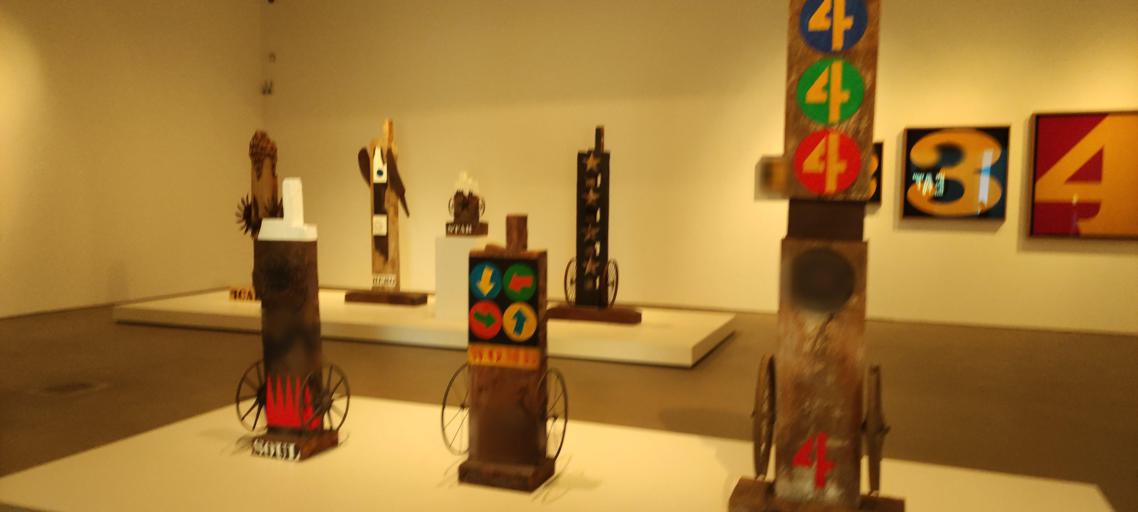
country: GB
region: England
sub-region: Kirklees
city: Clayton West
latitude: 53.6142
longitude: -1.5709
